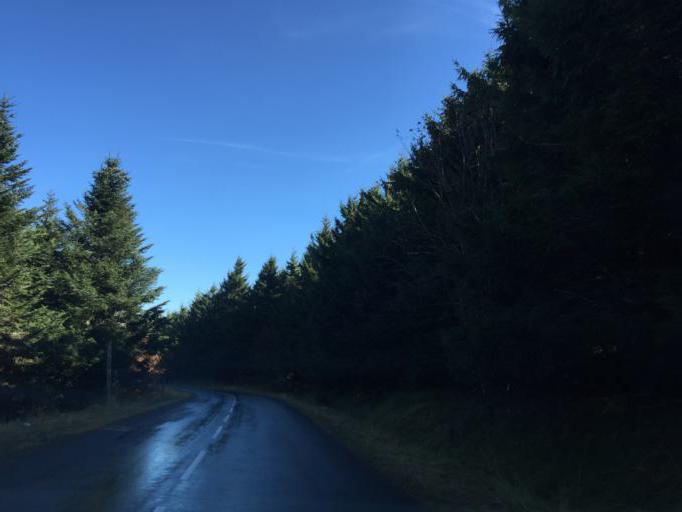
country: FR
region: Rhone-Alpes
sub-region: Departement de la Loire
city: Saint-Julien-Molin-Molette
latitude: 45.3860
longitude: 4.5736
